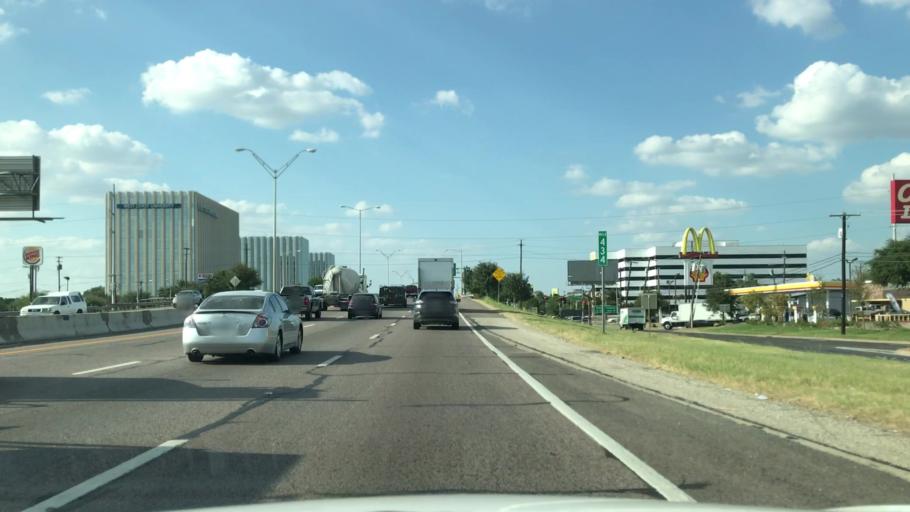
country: US
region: Texas
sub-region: Dallas County
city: University Park
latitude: 32.8249
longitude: -96.8715
